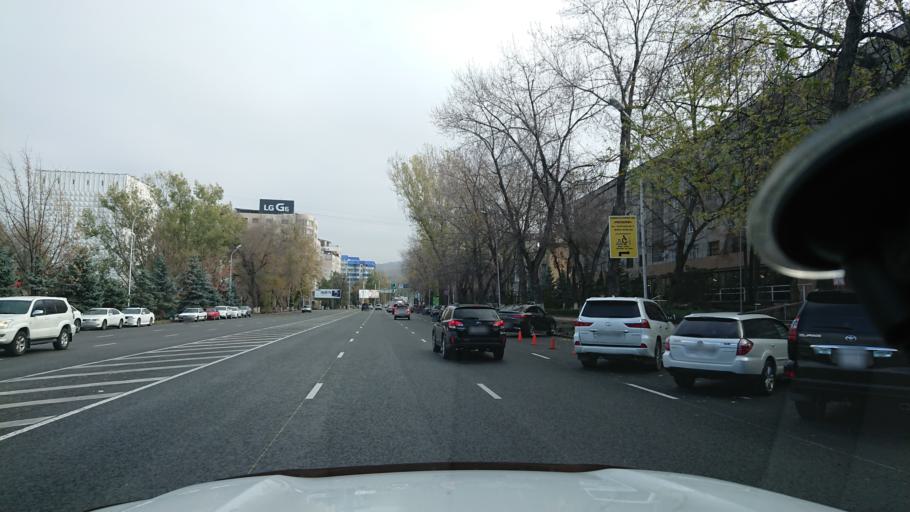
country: KZ
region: Almaty Qalasy
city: Almaty
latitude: 43.2392
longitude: 76.9548
